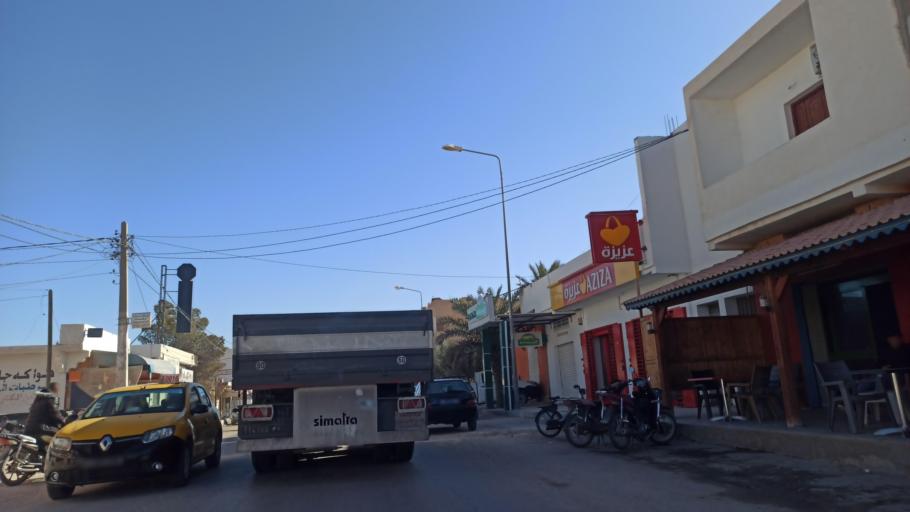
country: TN
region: Gafsa
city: Al Metlaoui
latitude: 34.3160
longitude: 8.3997
